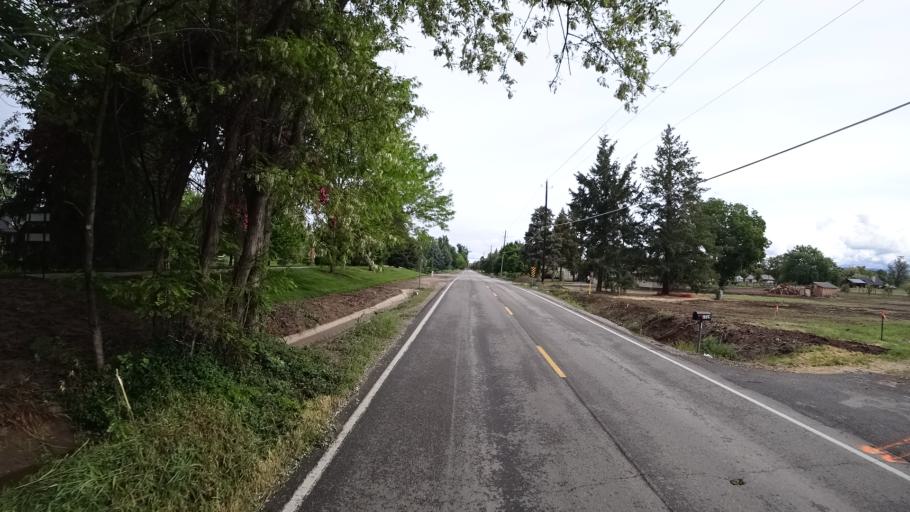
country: US
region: Idaho
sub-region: Ada County
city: Eagle
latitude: 43.7101
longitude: -116.3791
